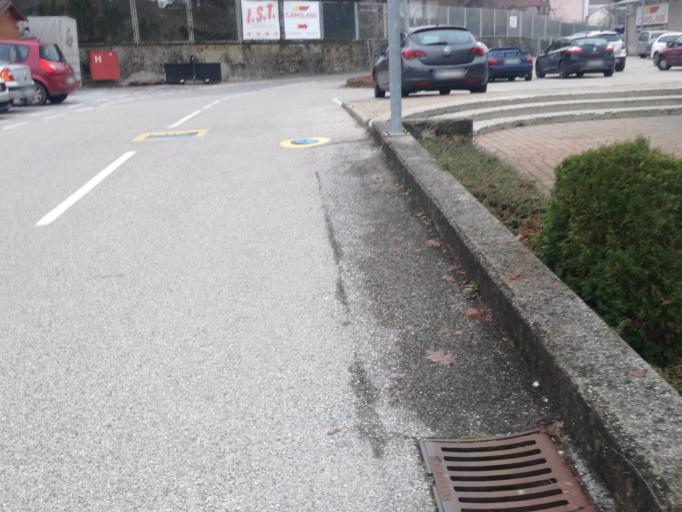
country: SI
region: Novo Mesto
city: Novo Mesto
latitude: 45.8178
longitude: 15.1558
